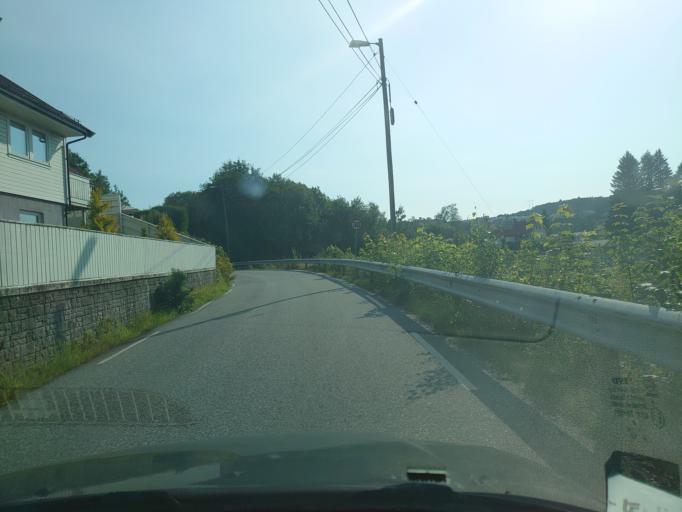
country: NO
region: Hordaland
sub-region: Bergen
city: Ytrebygda
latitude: 60.3353
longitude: 5.2841
